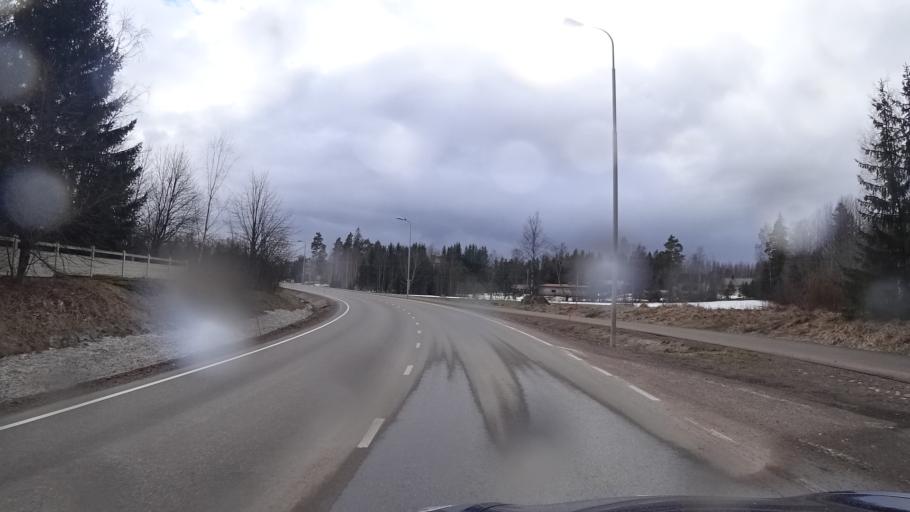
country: FI
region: Kymenlaakso
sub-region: Kotka-Hamina
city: Karhula
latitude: 60.5397
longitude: 26.9037
